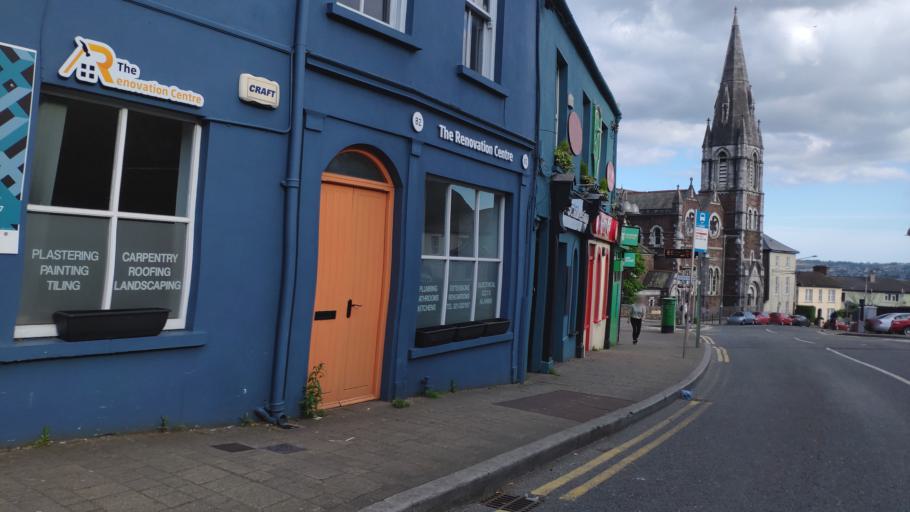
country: IE
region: Munster
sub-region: County Cork
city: Cork
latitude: 51.9050
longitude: -8.4578
